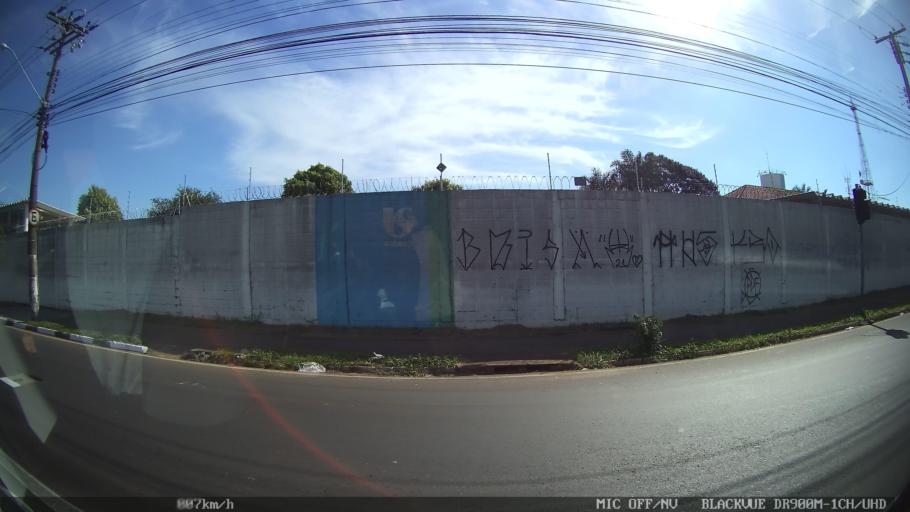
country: BR
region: Sao Paulo
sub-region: Franca
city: Franca
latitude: -20.5072
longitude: -47.3998
